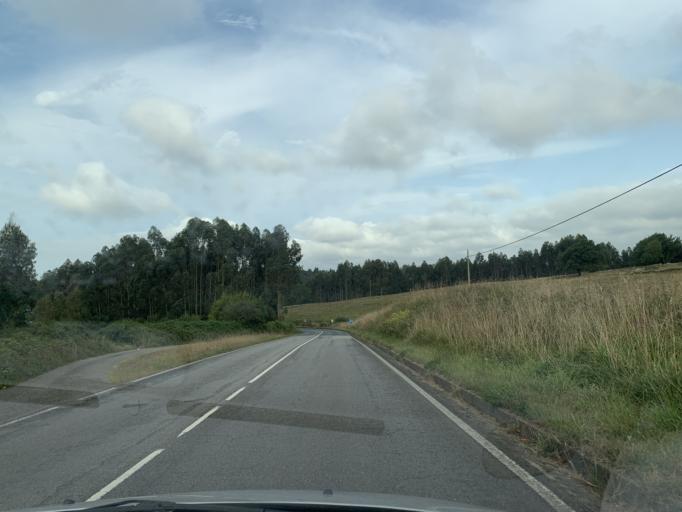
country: ES
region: Asturias
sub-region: Province of Asturias
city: Villaviciosa
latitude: 43.5167
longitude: -5.4305
